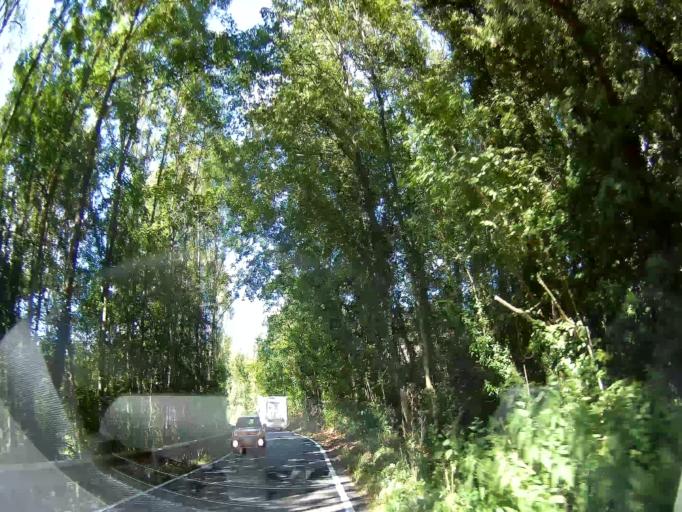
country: BE
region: Wallonia
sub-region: Province de Namur
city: Mettet
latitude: 50.3144
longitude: 4.7610
